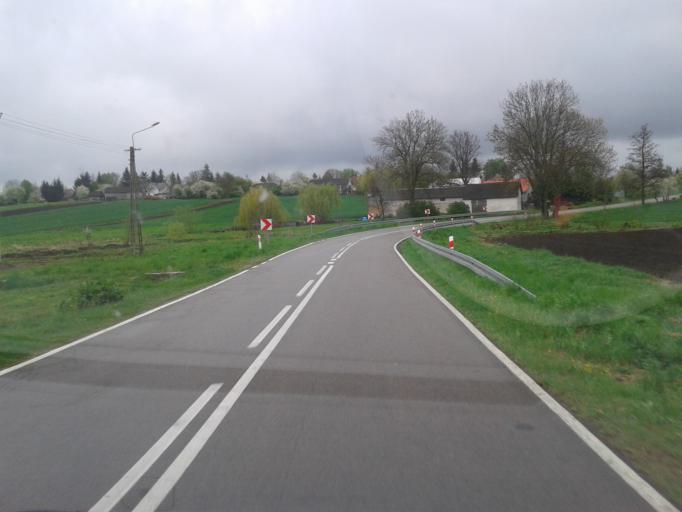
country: PL
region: Lublin Voivodeship
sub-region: Powiat hrubieszowski
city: Dolhobyczow
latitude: 50.5867
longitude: 23.9711
